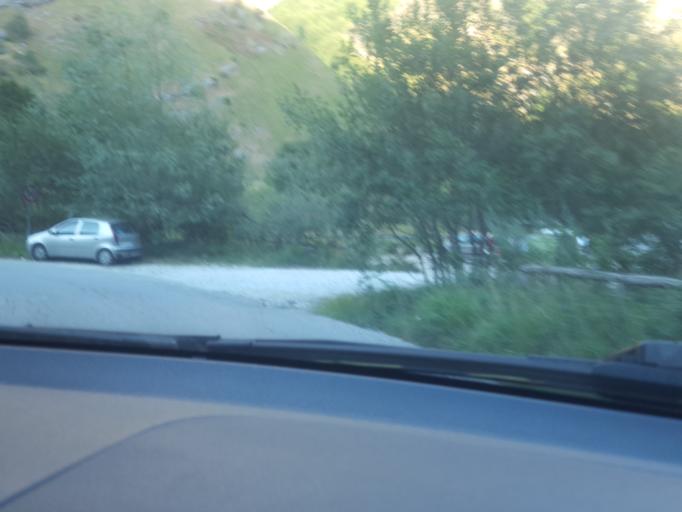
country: IT
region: Tuscany
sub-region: Provincia di Lucca
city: Minucciano
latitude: 44.1327
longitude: 10.1986
